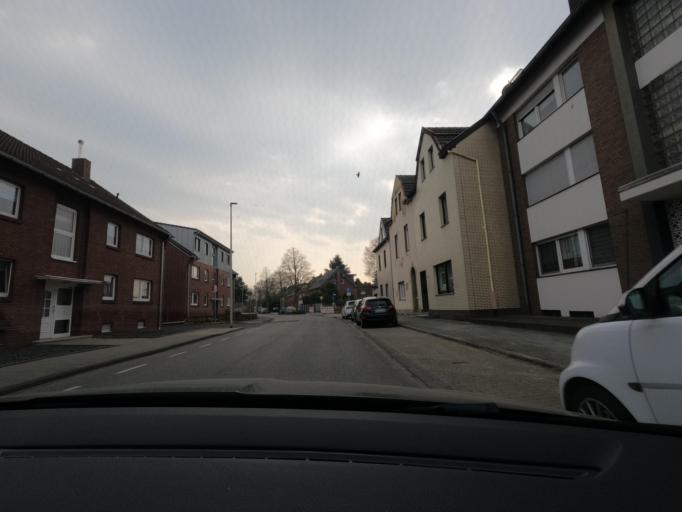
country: DE
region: North Rhine-Westphalia
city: Wegberg
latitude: 51.1388
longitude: 6.2838
